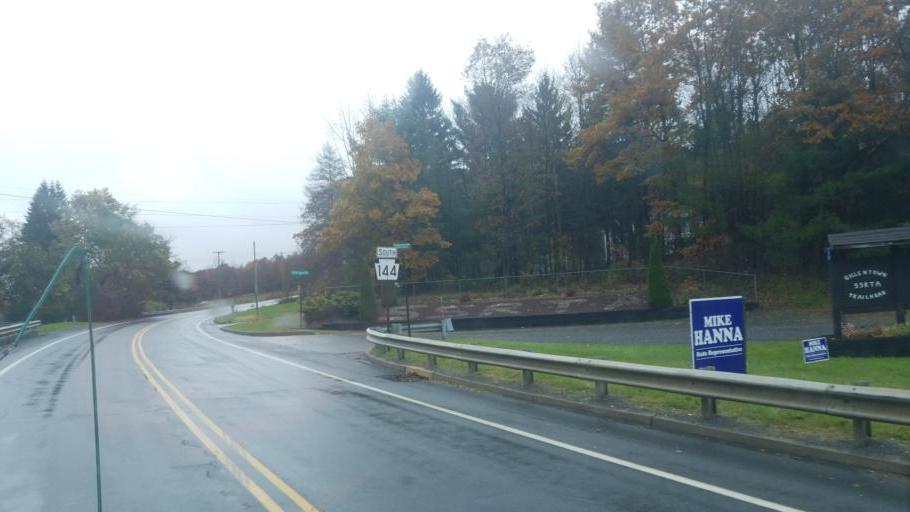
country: US
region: Pennsylvania
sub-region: Centre County
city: Milesburg
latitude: 41.0326
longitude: -77.9910
